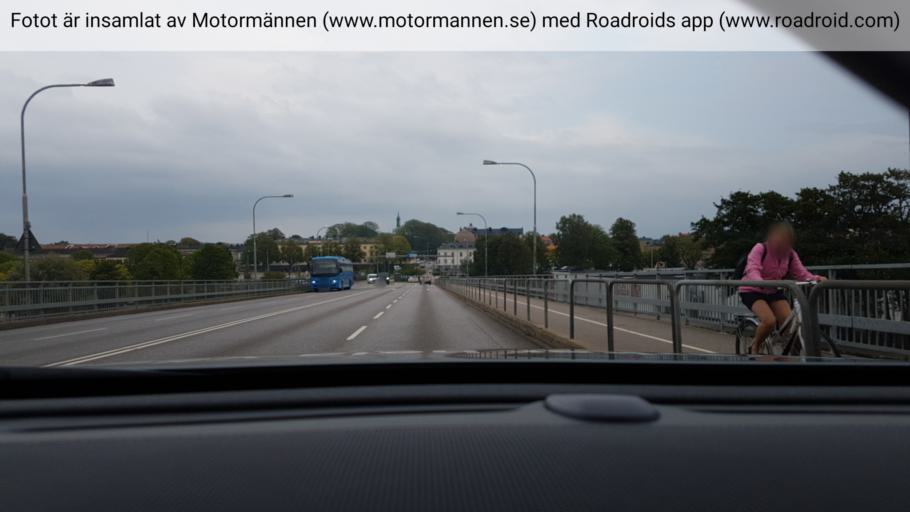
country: SE
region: Vaestra Goetaland
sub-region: Vanersborgs Kommun
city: Vanersborg
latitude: 58.3821
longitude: 12.3144
